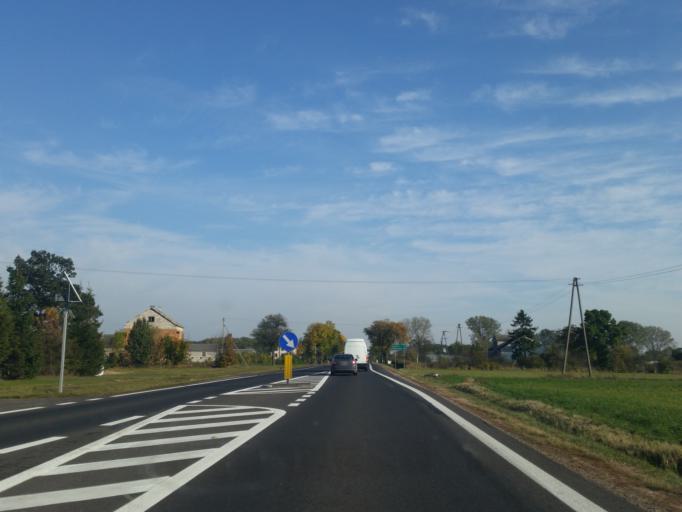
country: PL
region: Masovian Voivodeship
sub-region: Powiat sierpecki
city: Zawidz
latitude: 52.8120
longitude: 19.8101
